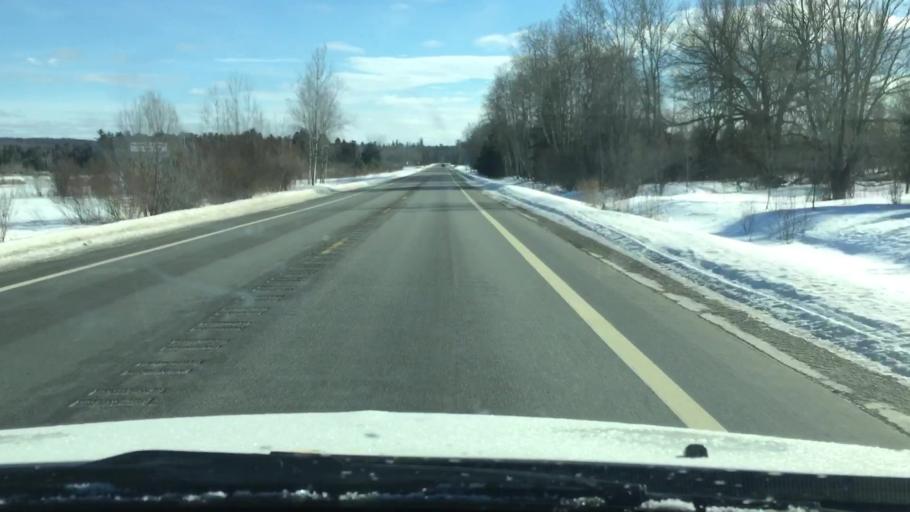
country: US
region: Michigan
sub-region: Charlevoix County
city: East Jordan
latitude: 45.0637
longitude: -85.0809
